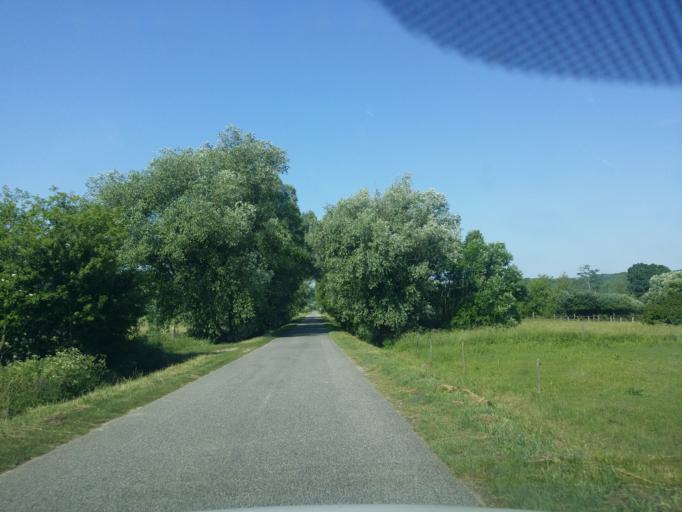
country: HU
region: Zala
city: Zalaszentgrot
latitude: 46.8894
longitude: 17.0966
